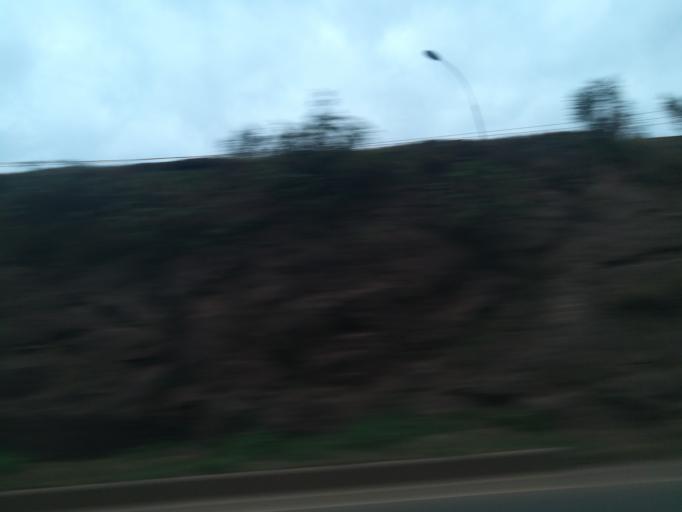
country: KE
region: Nairobi Area
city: Thika
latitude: -1.1077
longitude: 37.0142
